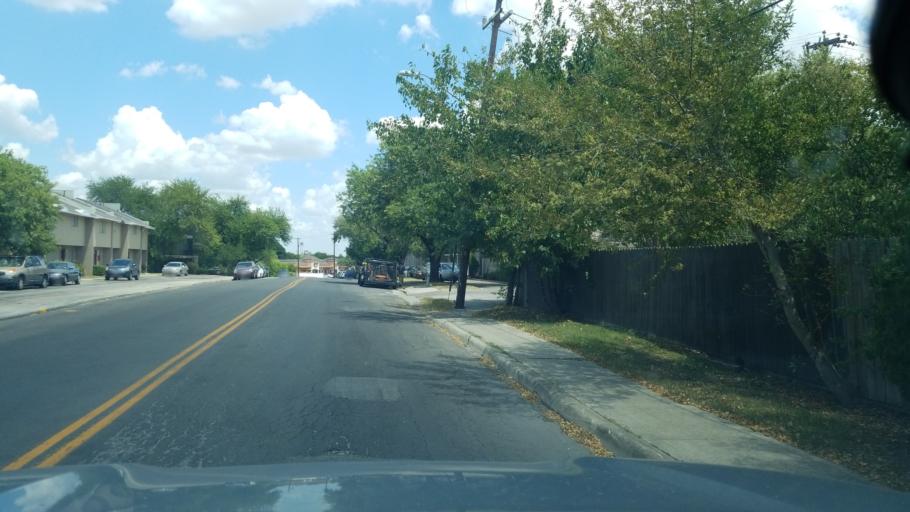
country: US
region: Texas
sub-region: Bexar County
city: Castle Hills
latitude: 29.5279
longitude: -98.5024
